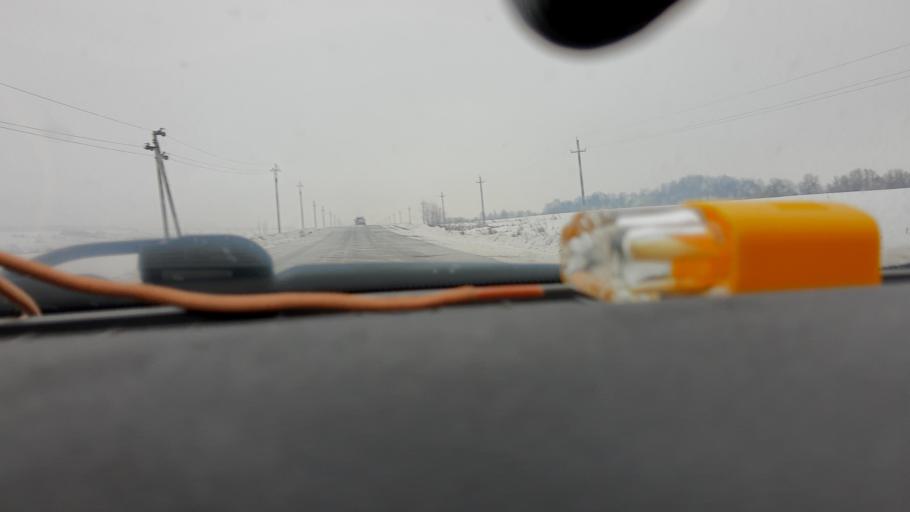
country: RU
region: Bashkortostan
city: Ulukulevo
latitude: 54.5425
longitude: 56.4324
